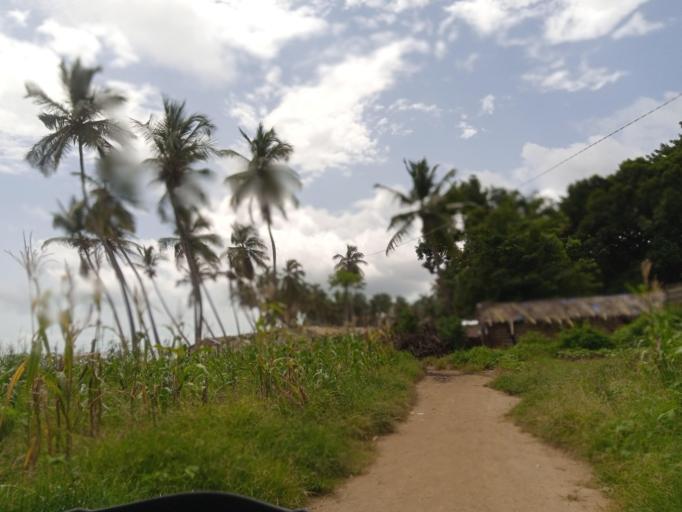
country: SL
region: Northern Province
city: Tintafor
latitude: 8.6210
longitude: -13.2143
